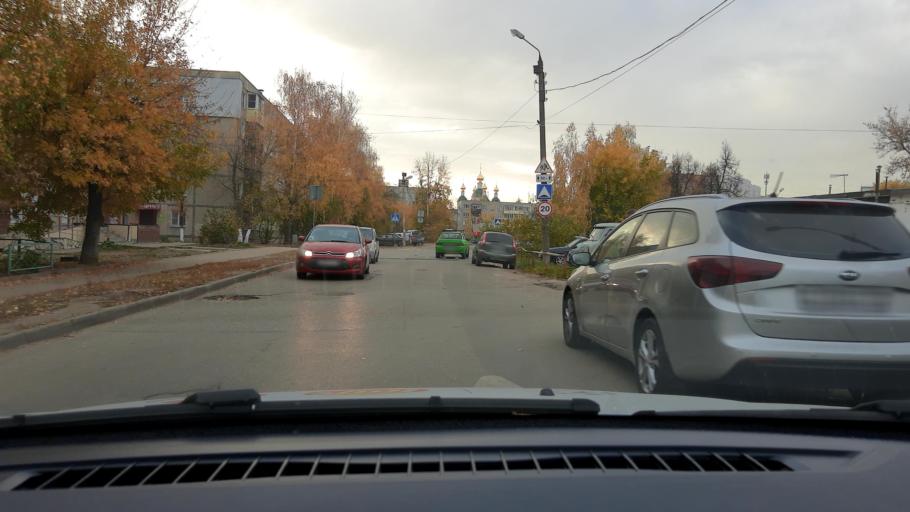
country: RU
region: Nizjnij Novgorod
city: Burevestnik
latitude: 56.2251
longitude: 43.8644
